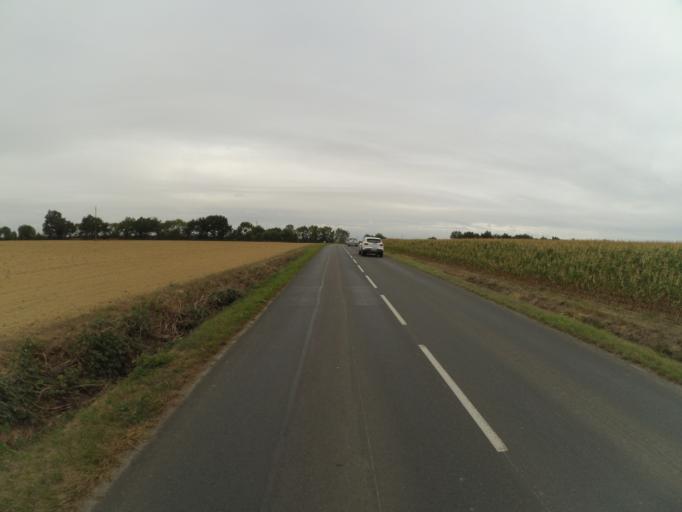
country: FR
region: Pays de la Loire
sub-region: Departement de la Vendee
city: Saint-Andre-Treize-Voies
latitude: 46.9243
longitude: -1.3969
